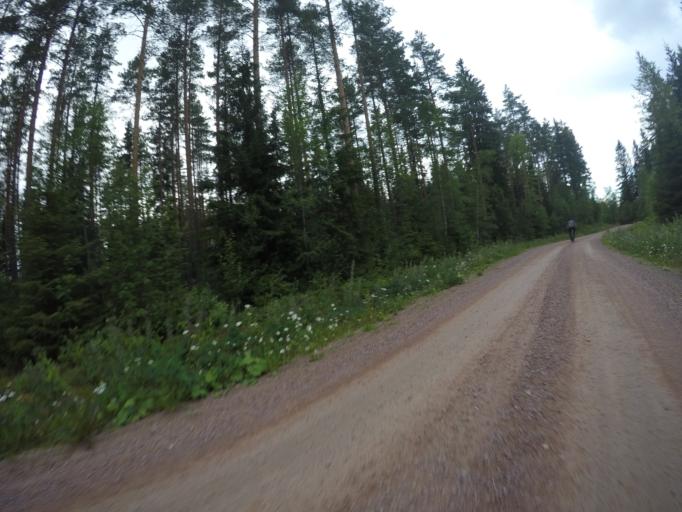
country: SE
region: OErebro
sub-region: Hallefors Kommun
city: Haellefors
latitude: 60.0411
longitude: 14.5024
